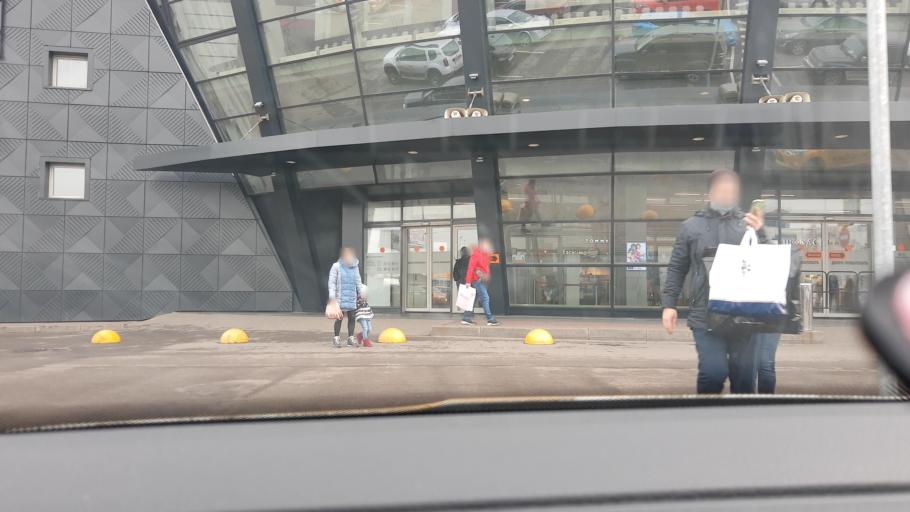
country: RU
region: Moskovskaya
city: Druzhba
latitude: 55.8921
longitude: 37.7478
